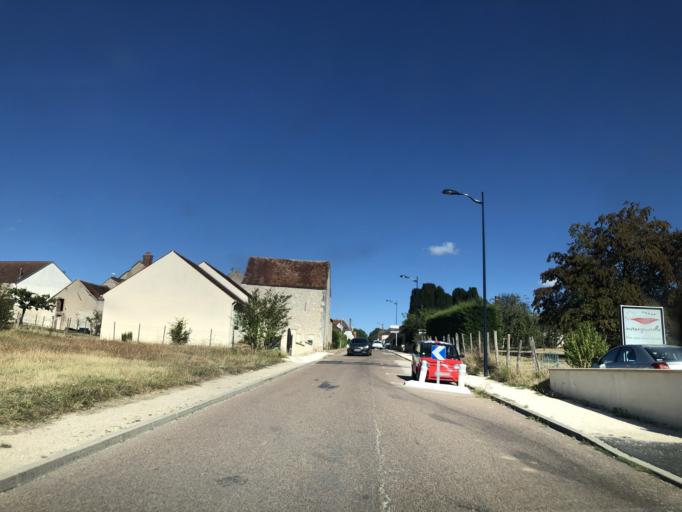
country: FR
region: Bourgogne
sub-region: Departement de l'Yonne
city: Gurgy
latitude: 47.8988
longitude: 3.5578
